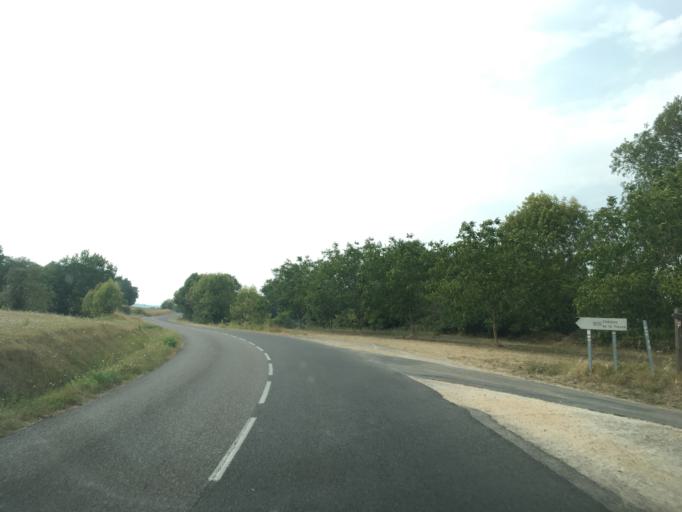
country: FR
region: Midi-Pyrenees
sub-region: Departement du Lot
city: Souillac
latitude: 44.8442
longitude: 1.5479
